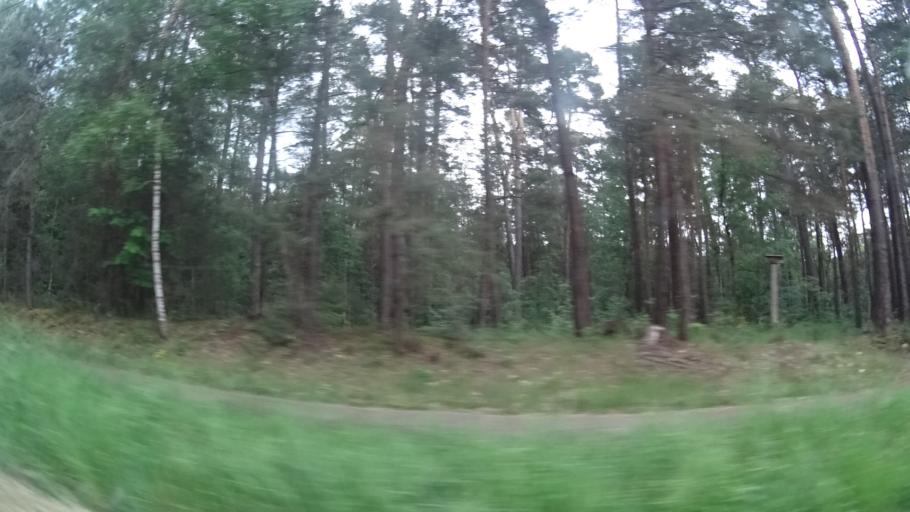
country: DE
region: Rheinland-Pfalz
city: Dudenhofen
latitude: 49.3353
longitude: 8.3735
